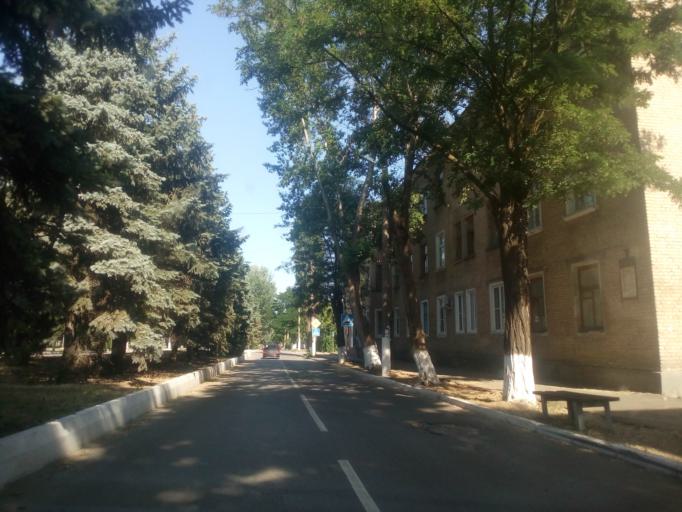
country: RU
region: Rostov
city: Sholokhovskiy
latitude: 48.2818
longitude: 41.0492
